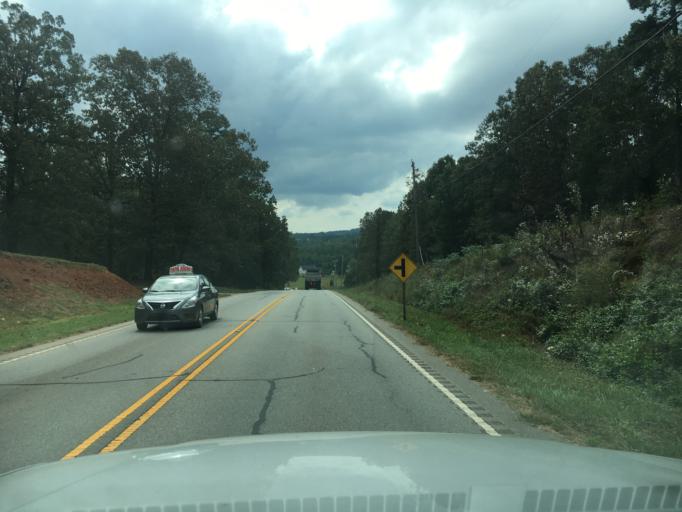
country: US
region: South Carolina
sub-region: Greenville County
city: Greer
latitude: 34.9879
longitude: -82.2456
